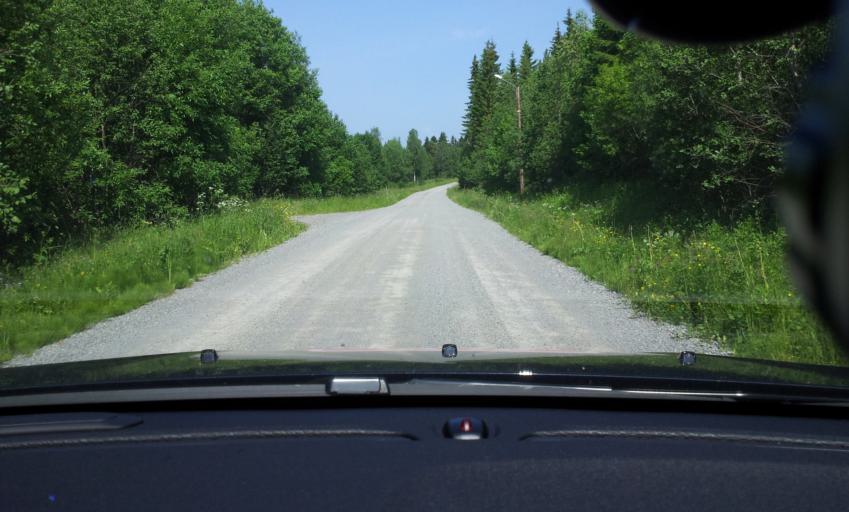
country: SE
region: Jaemtland
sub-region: Bergs Kommun
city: Hoverberg
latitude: 62.7749
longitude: 14.4445
